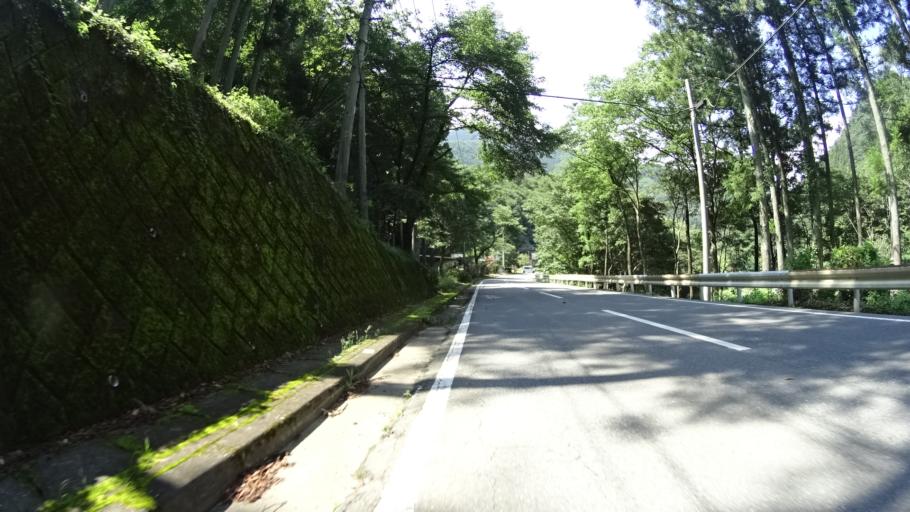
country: JP
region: Gunma
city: Tomioka
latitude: 36.0818
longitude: 138.7996
